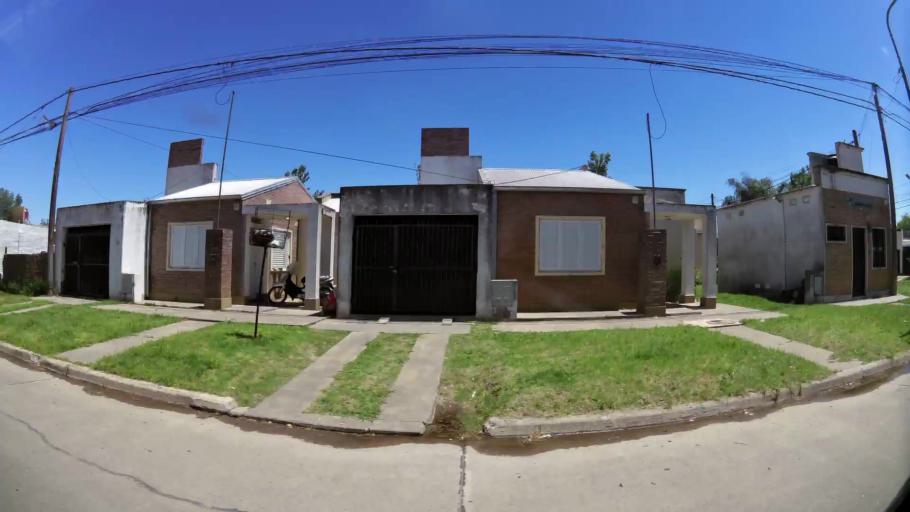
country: AR
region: Santa Fe
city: Rafaela
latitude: -31.2520
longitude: -61.4564
